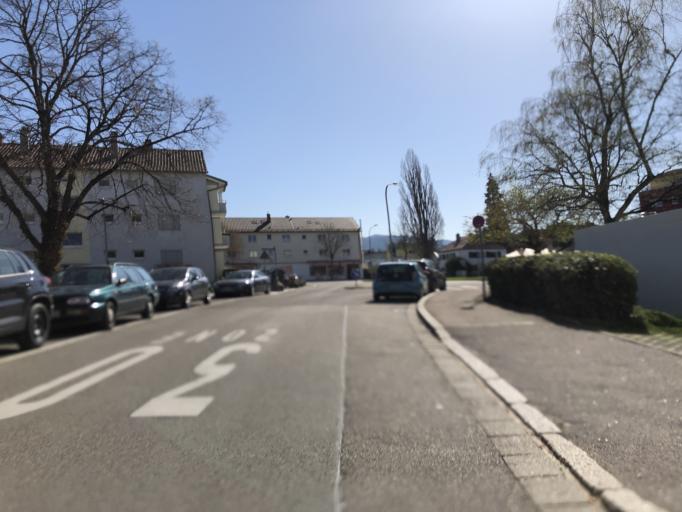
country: DE
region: Baden-Wuerttemberg
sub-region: Freiburg Region
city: Merzhausen
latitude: 47.9943
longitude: 7.8211
